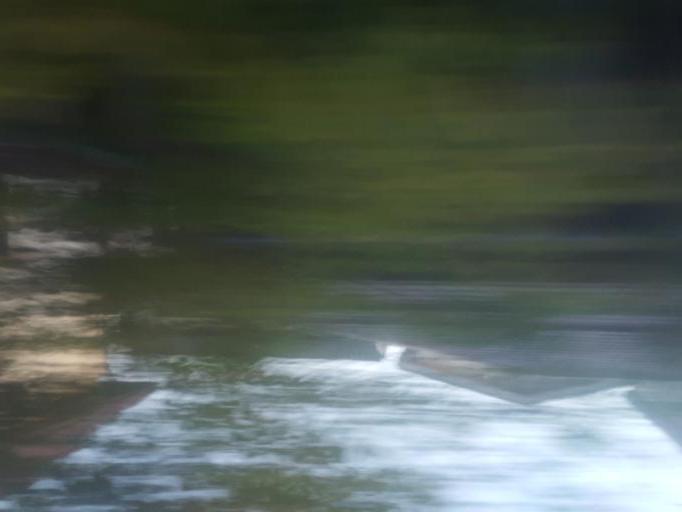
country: JP
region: Toyama
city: Toyama-shi
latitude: 36.6988
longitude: 137.2599
